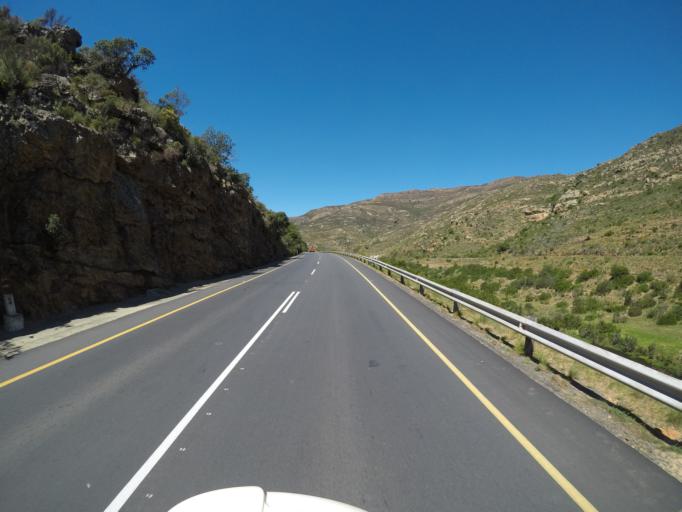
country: ZA
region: Western Cape
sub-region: Cape Winelands District Municipality
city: Ceres
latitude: -33.3145
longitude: 19.0761
